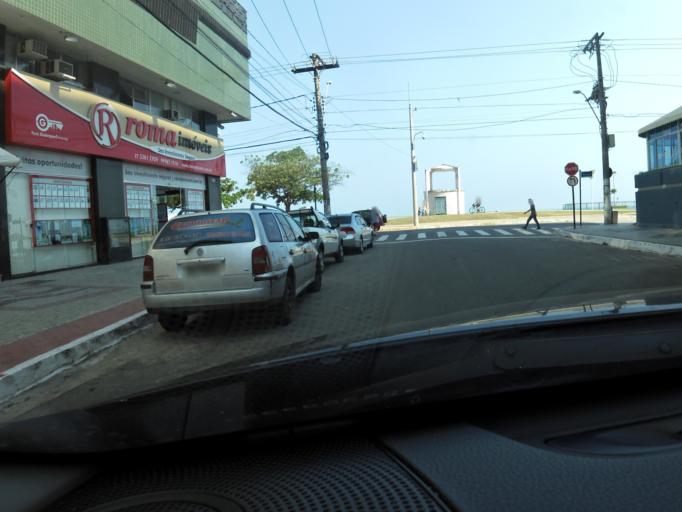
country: BR
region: Espirito Santo
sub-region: Guarapari
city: Guarapari
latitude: -20.6528
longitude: -40.4853
